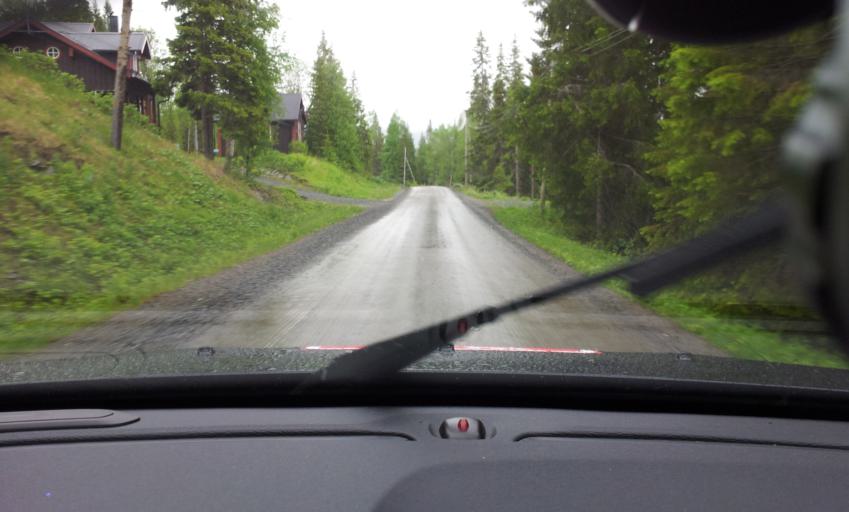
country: SE
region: Jaemtland
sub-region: Are Kommun
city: Are
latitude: 63.5077
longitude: 12.7274
